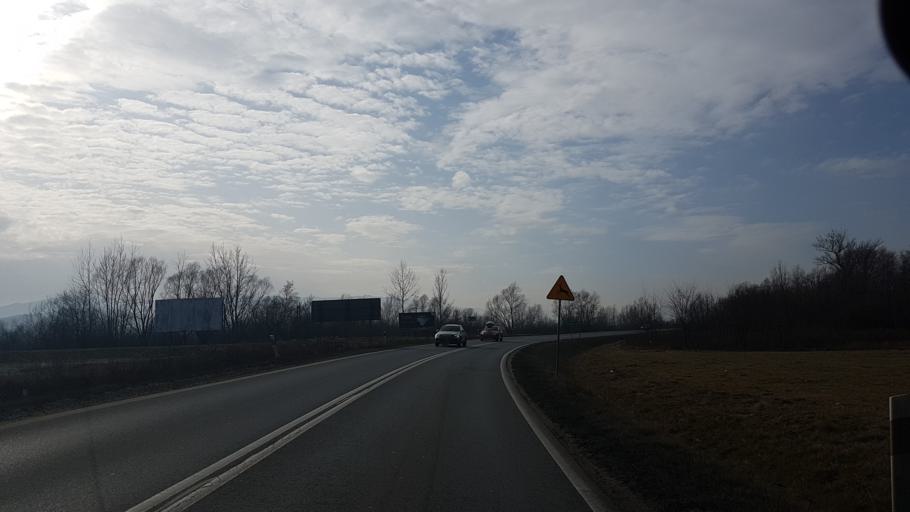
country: PL
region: Lesser Poland Voivodeship
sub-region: Powiat nowosadecki
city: Stary Sacz
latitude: 49.5879
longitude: 20.6294
